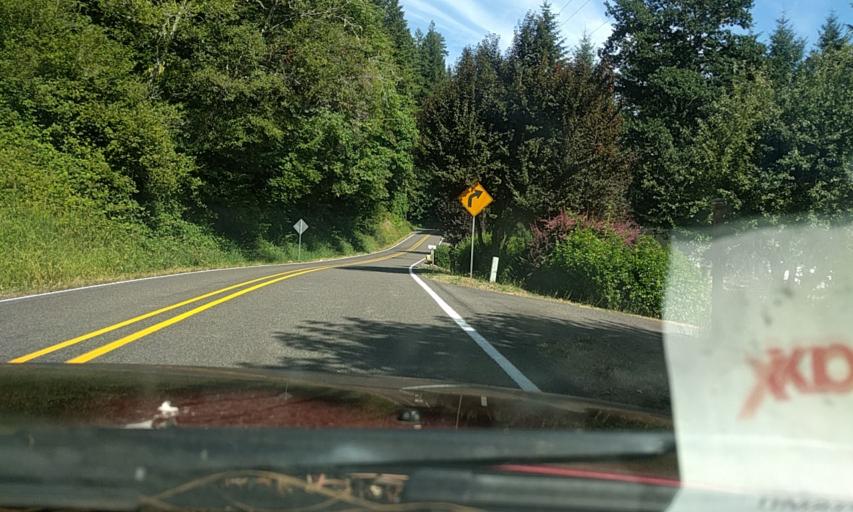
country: US
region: Oregon
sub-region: Lane County
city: Florence
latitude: 44.0420
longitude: -123.8670
